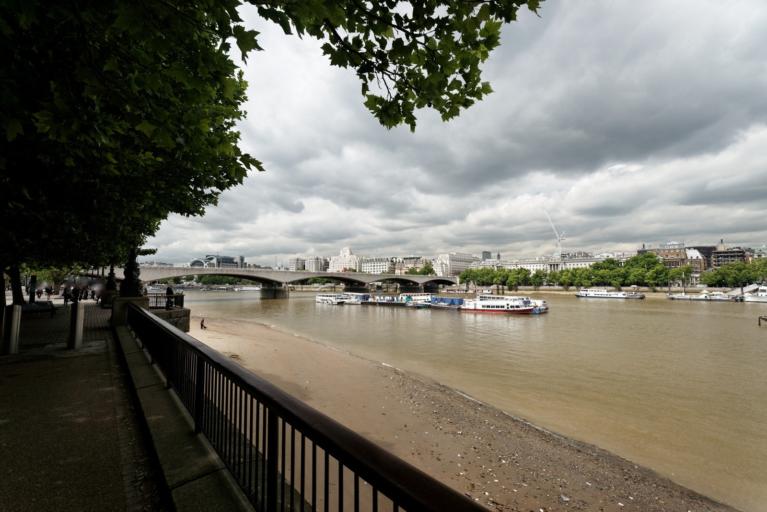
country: GB
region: England
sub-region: Greater London
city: City of Westminster
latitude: 51.5081
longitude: -0.1132
